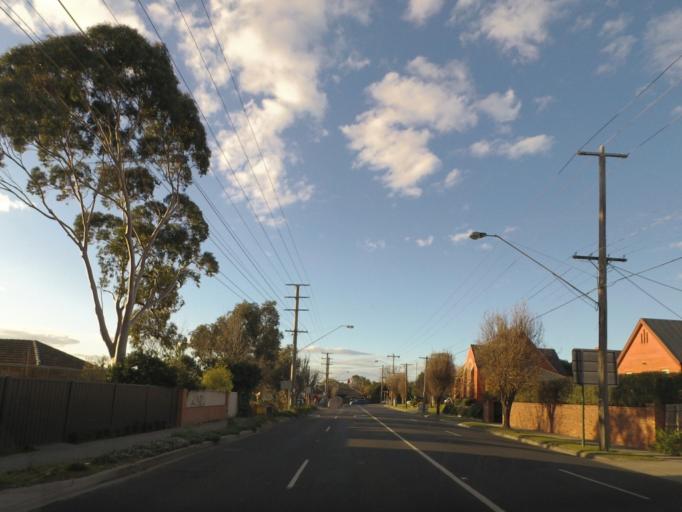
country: AU
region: Victoria
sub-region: Whitehorse
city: Surrey Hills
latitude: -37.8272
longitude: 145.0997
